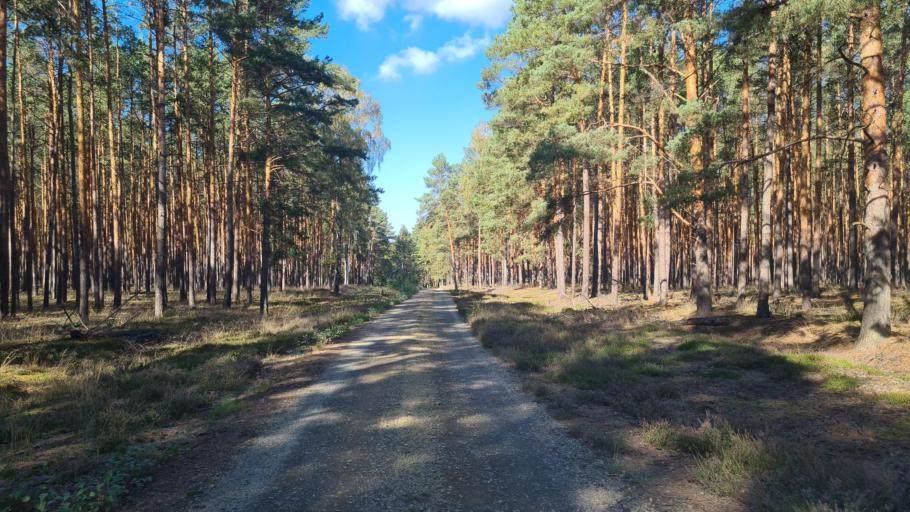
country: DE
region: Brandenburg
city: Lebusa
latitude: 51.8339
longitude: 13.4983
